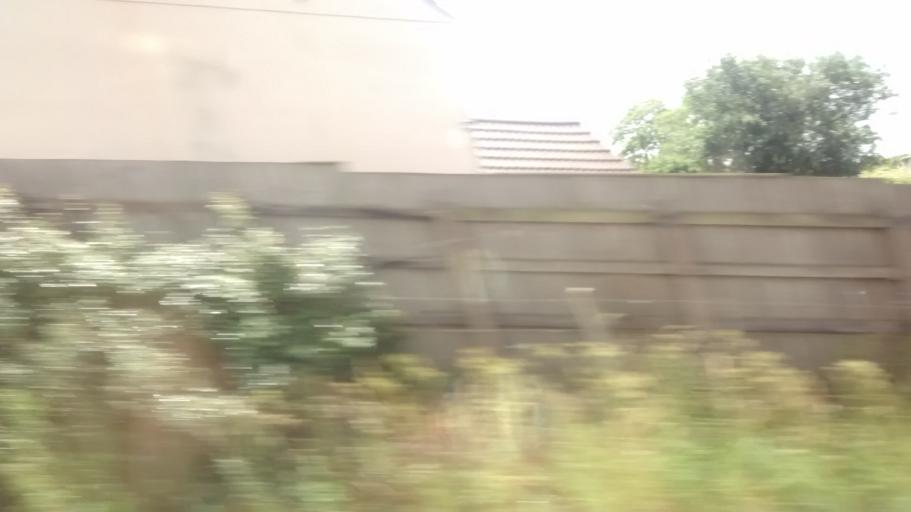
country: GB
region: England
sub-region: Nottinghamshire
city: Newark on Trent
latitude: 53.0611
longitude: -0.7748
